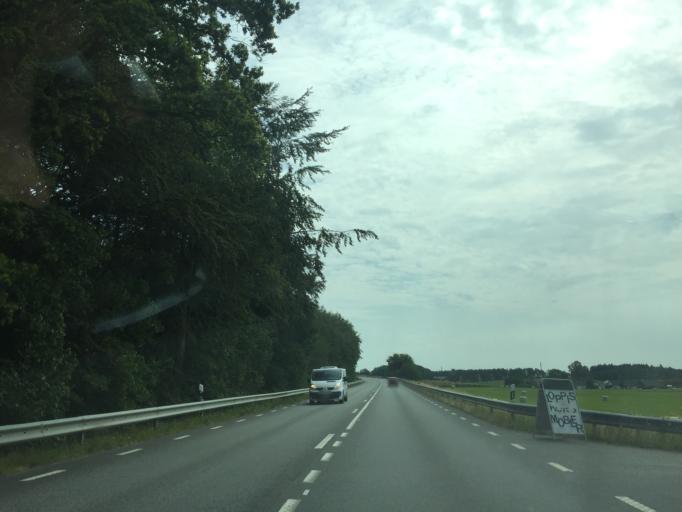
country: SE
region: Skane
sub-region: Sjobo Kommun
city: Sjoebo
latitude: 55.6047
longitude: 13.7844
